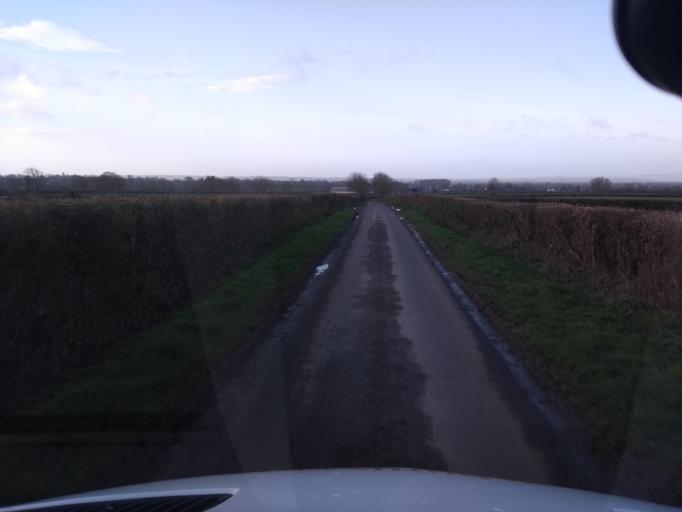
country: GB
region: England
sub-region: Somerset
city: Wedmore
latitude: 51.2345
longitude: -2.8330
